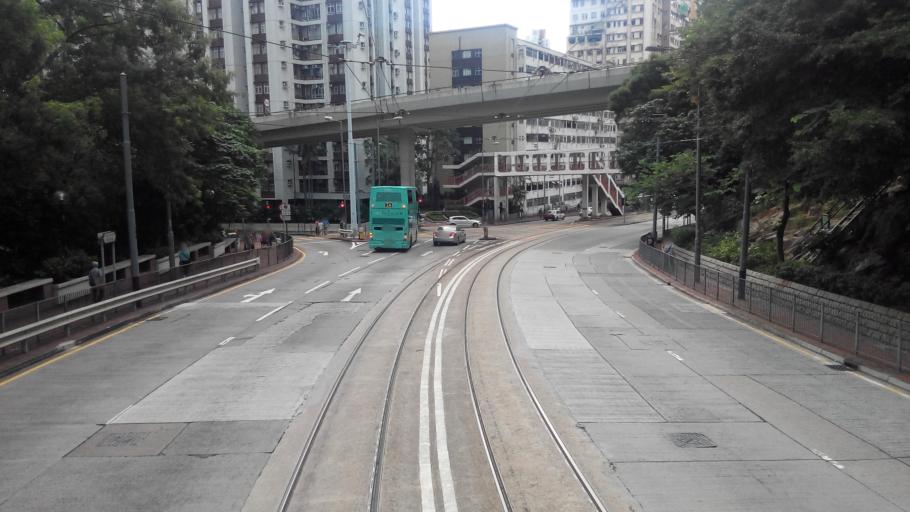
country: HK
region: Wanchai
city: Wan Chai
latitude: 22.2848
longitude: 114.2195
